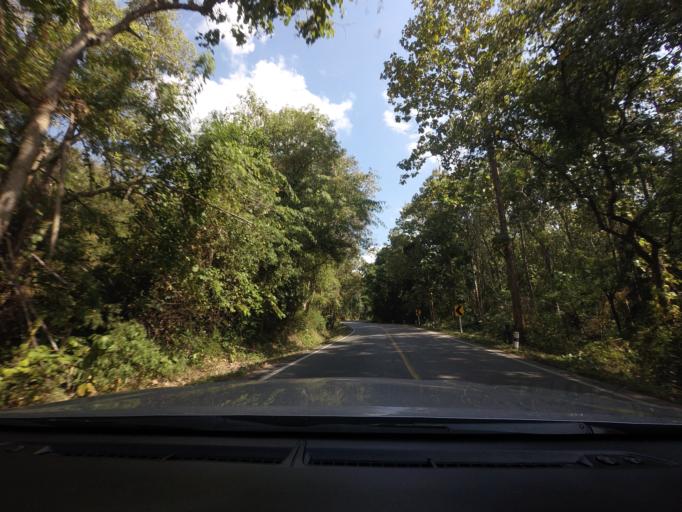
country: TH
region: Chiang Mai
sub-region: Amphoe Chiang Dao
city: Chiang Dao
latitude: 19.4790
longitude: 99.0090
